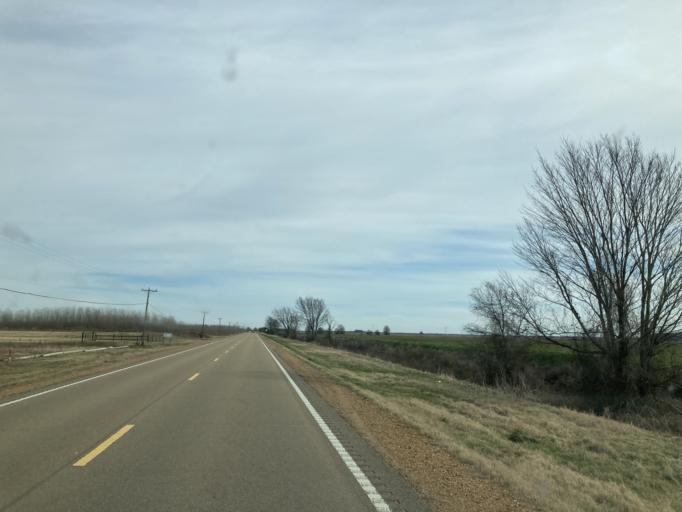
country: US
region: Mississippi
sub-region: Humphreys County
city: Belzoni
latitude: 33.1833
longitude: -90.6043
